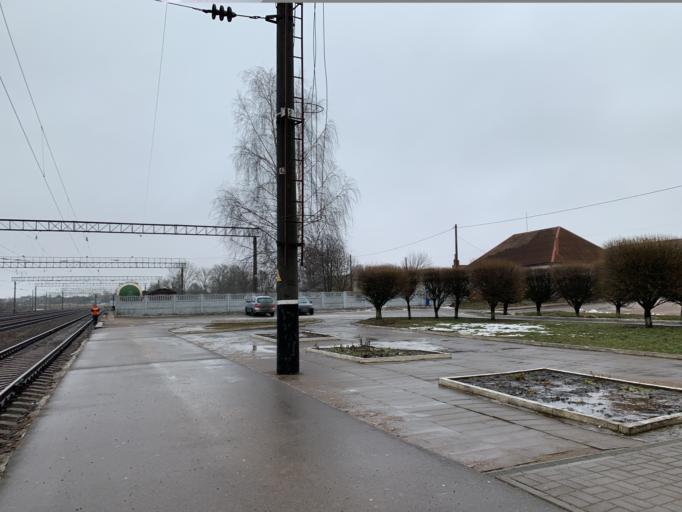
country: BY
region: Minsk
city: Haradzyeya
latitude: 53.3150
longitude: 26.5383
